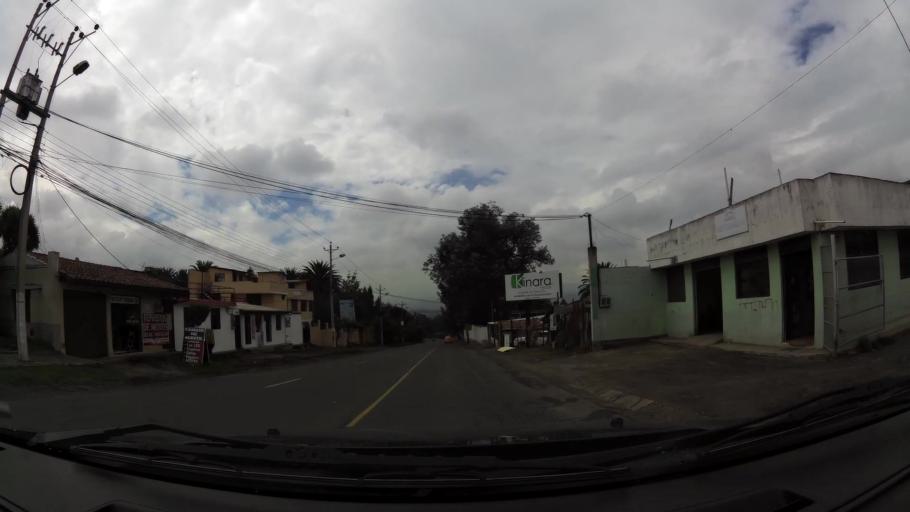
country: EC
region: Pichincha
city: Sangolqui
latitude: -0.3043
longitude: -78.4780
